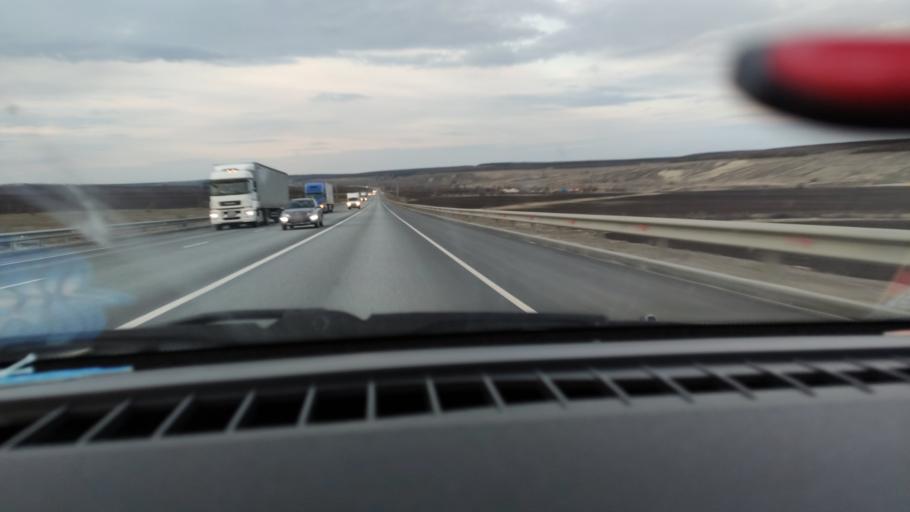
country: RU
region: Saratov
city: Yelshanka
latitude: 51.8445
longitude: 46.4827
